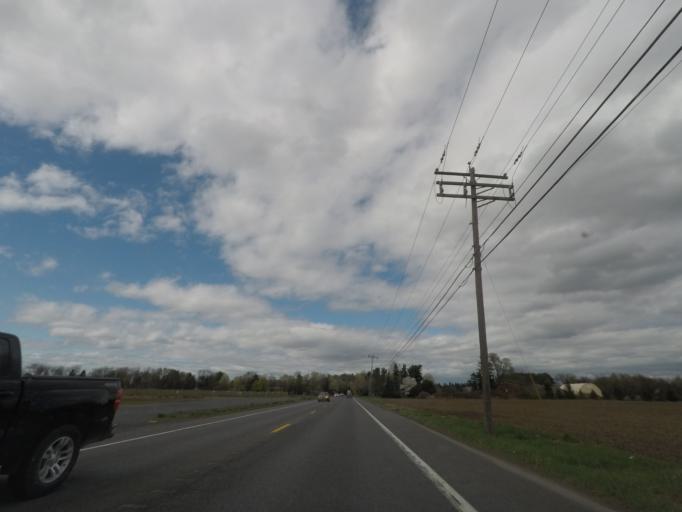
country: US
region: New York
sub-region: Columbia County
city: Niverville
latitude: 42.4414
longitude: -73.6865
